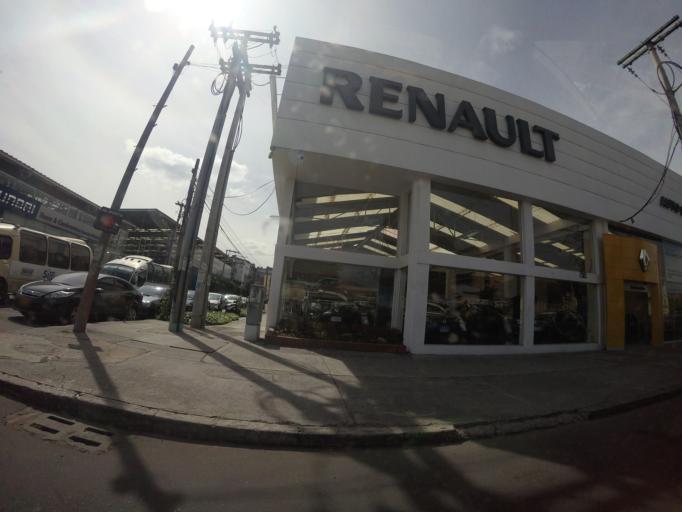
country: CO
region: Bogota D.C.
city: Barrio San Luis
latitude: 4.6936
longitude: -74.0759
